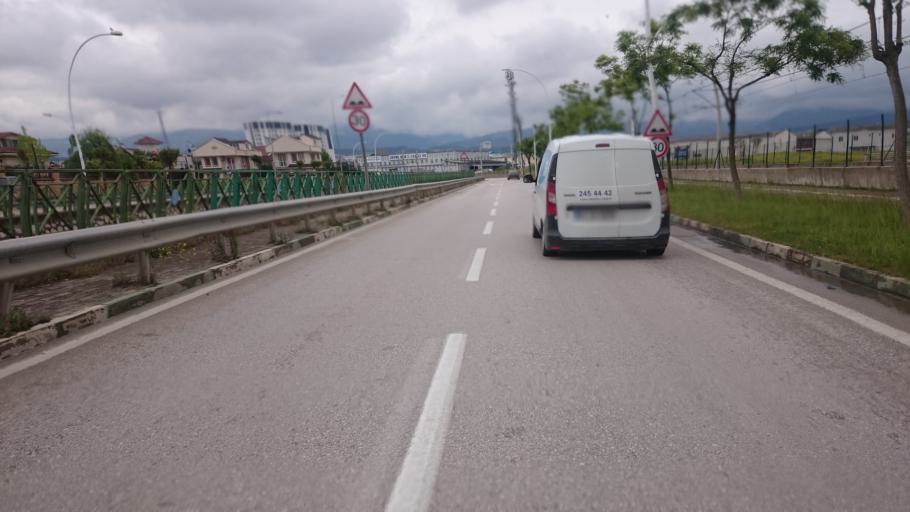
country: TR
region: Bursa
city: Cali
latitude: 40.2179
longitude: 28.9297
